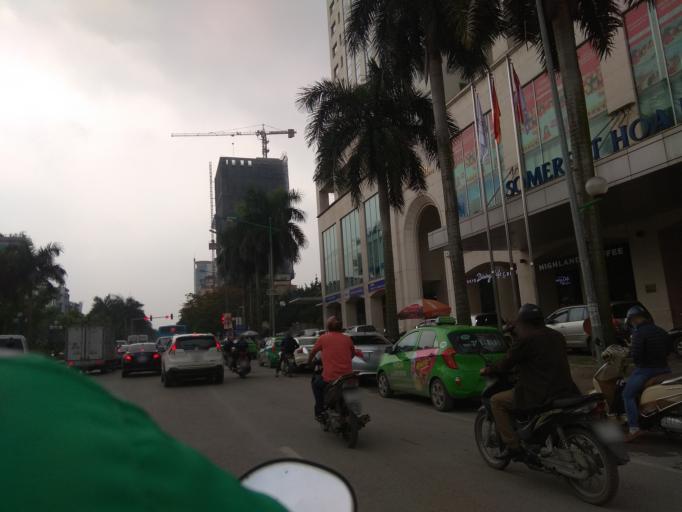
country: VN
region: Ha Noi
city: Cau Giay
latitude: 21.0463
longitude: 105.7955
